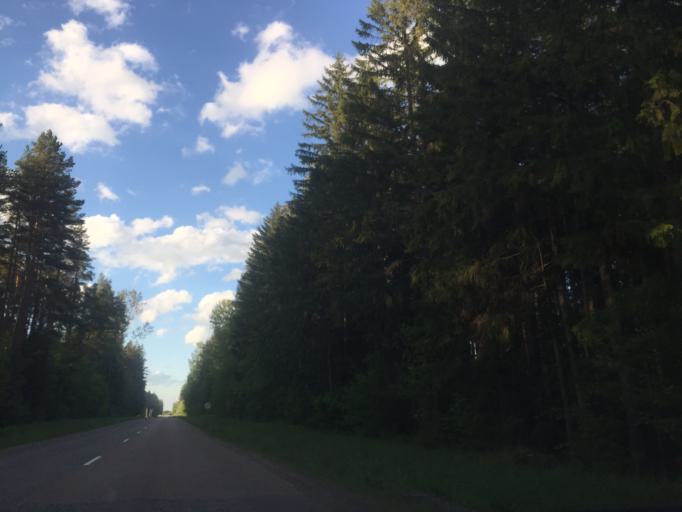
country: LV
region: Kandava
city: Kandava
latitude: 57.0057
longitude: 22.7803
